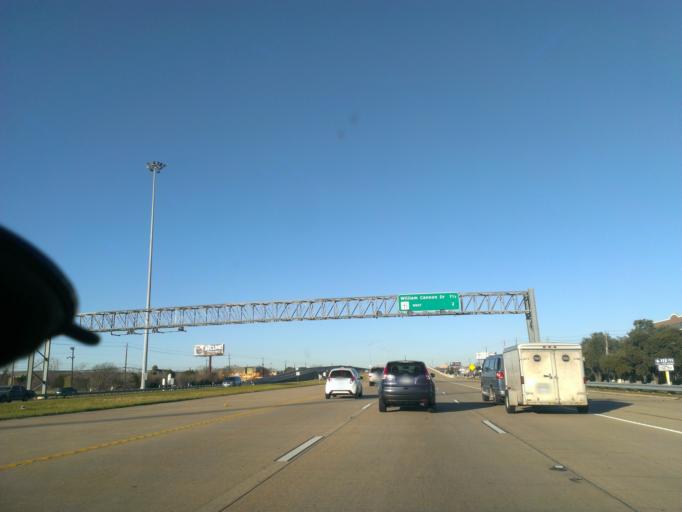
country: US
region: Texas
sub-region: Travis County
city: Rollingwood
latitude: 30.2369
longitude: -97.8330
